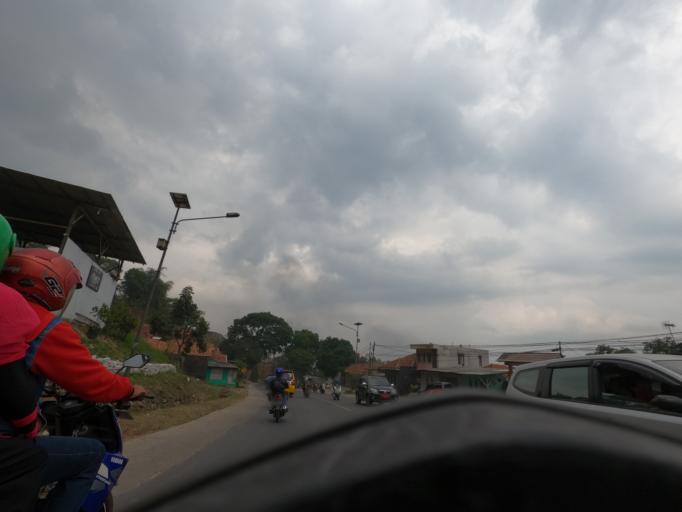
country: ID
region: West Java
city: Padalarang
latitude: -6.8318
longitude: 107.4440
